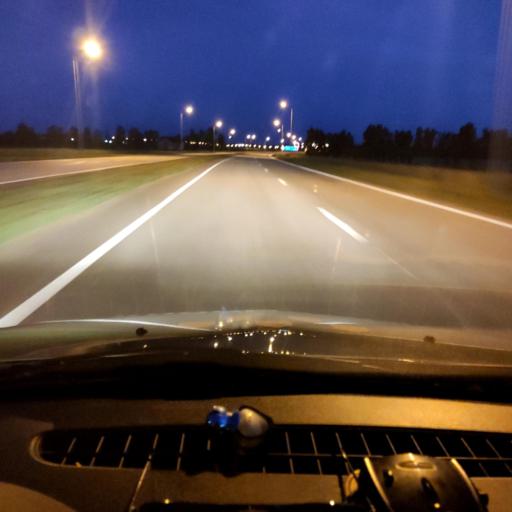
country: RU
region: Belgorod
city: Skorodnoye
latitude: 51.0823
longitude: 37.2129
